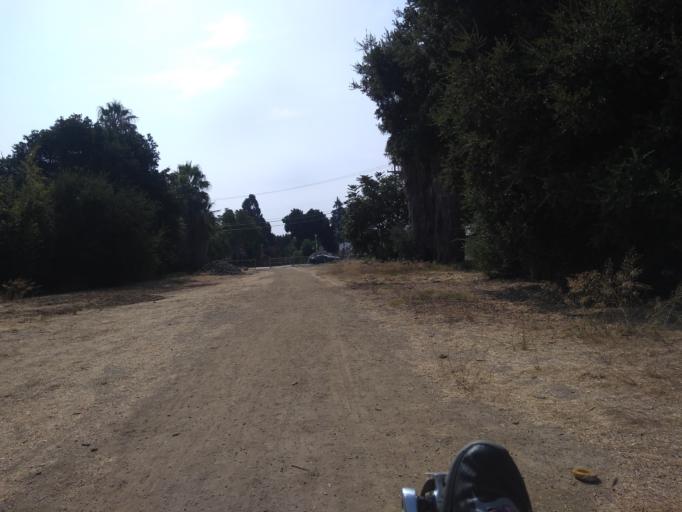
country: US
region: California
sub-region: Santa Clara County
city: Buena Vista
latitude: 37.3140
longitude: -121.9028
